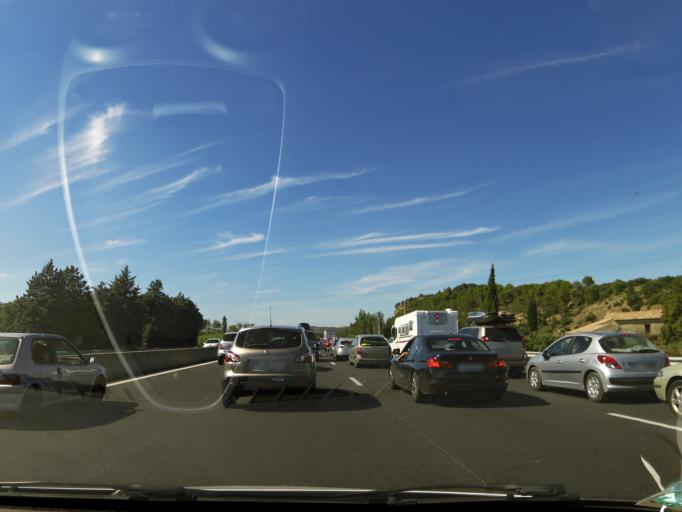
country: FR
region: Provence-Alpes-Cote d'Azur
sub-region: Departement du Vaucluse
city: Piolenc
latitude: 44.1641
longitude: 4.7657
